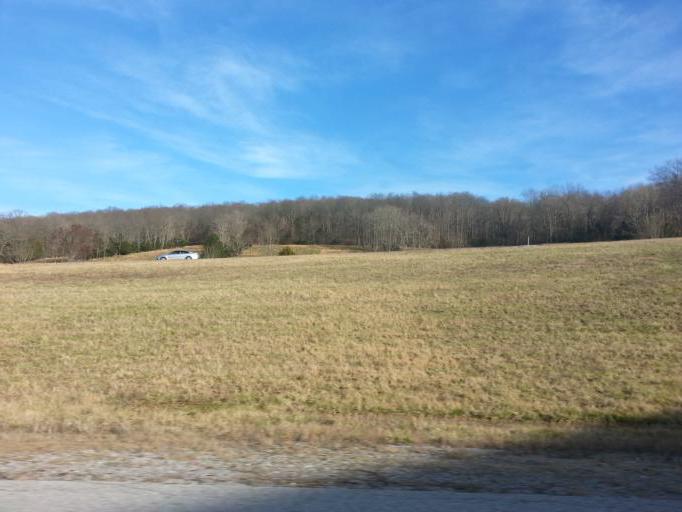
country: US
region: Tennessee
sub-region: White County
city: Sparta
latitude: 35.8729
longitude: -85.4705
